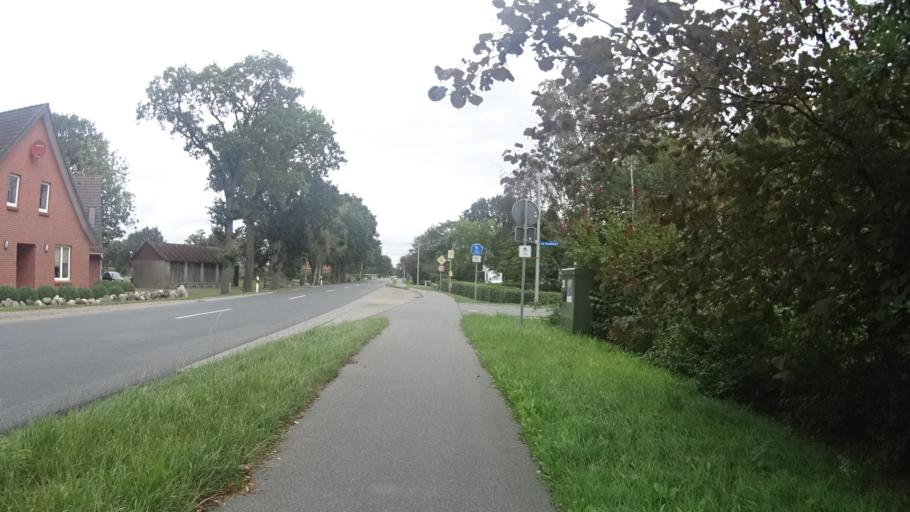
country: DE
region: Lower Saxony
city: Schiffdorf
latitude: 53.5442
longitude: 8.6823
